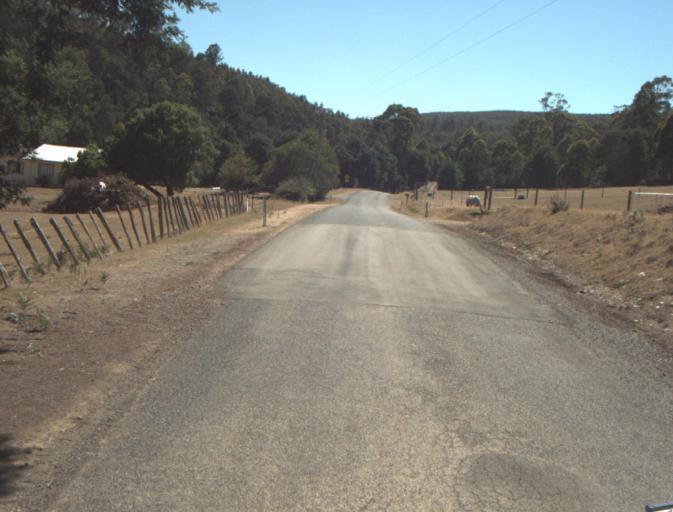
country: AU
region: Tasmania
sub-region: Launceston
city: Newstead
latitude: -41.2983
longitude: 147.3356
